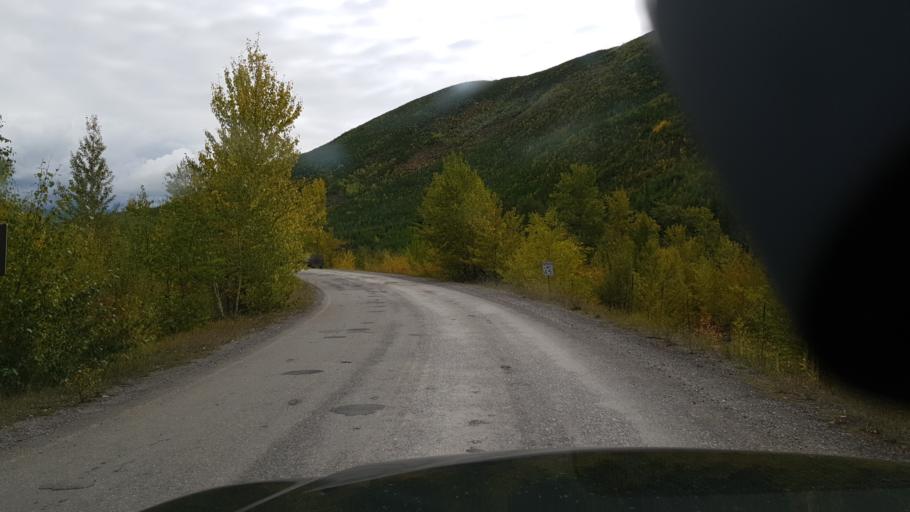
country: US
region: Montana
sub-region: Flathead County
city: Columbia Falls
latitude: 48.6204
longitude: -114.1409
